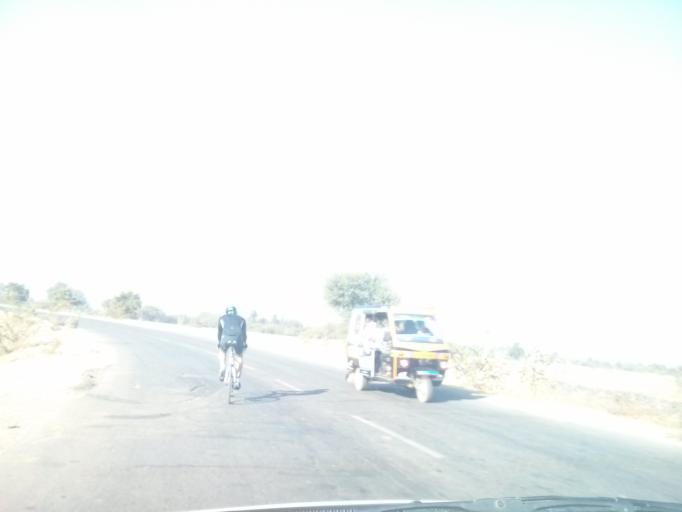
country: IN
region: Rajasthan
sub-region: Sirohi
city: Abu Road
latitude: 24.5571
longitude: 72.8315
